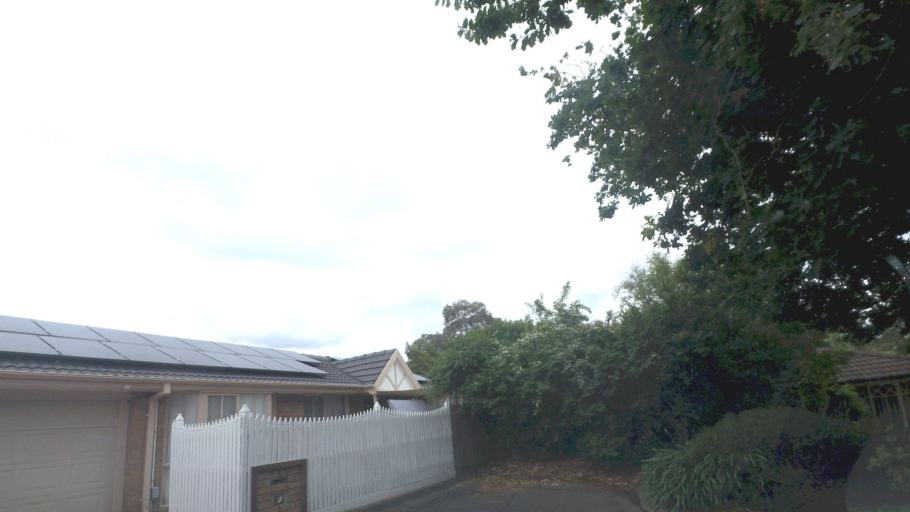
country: AU
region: Victoria
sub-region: Maroondah
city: Croydon South
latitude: -37.8145
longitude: 145.2816
